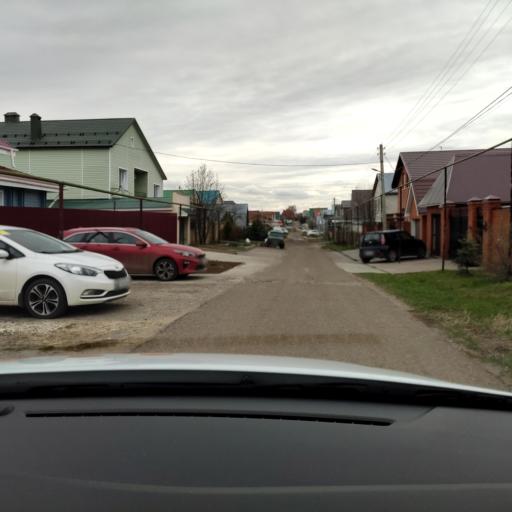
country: RU
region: Tatarstan
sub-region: Gorod Kazan'
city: Kazan
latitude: 55.6942
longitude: 49.1326
